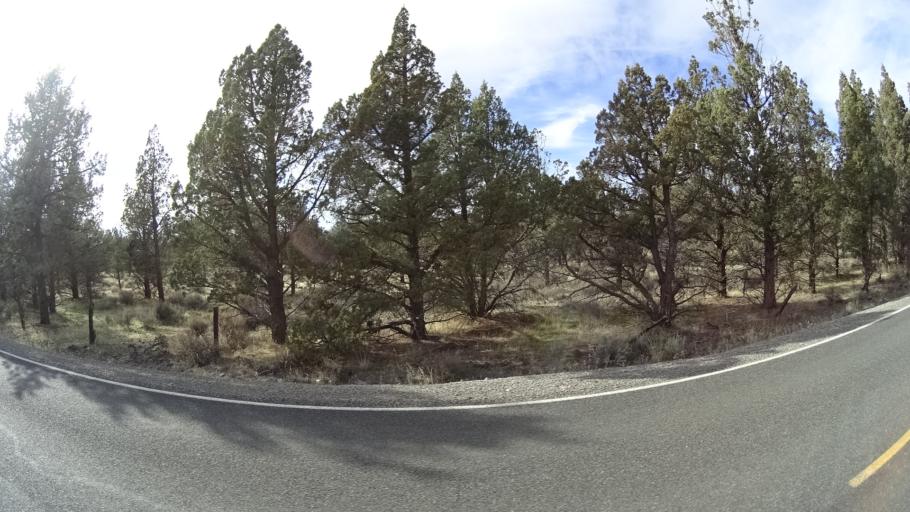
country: US
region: California
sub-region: Siskiyou County
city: Montague
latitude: 41.6503
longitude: -122.3994
